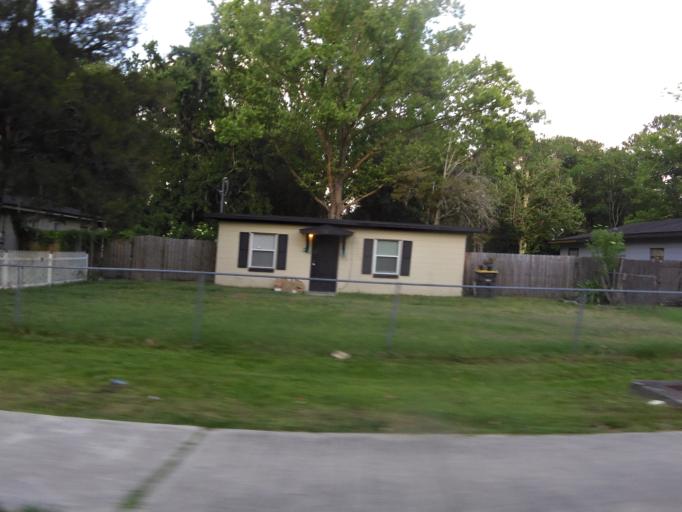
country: US
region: Florida
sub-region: Duval County
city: Jacksonville
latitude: 30.3041
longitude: -81.7393
